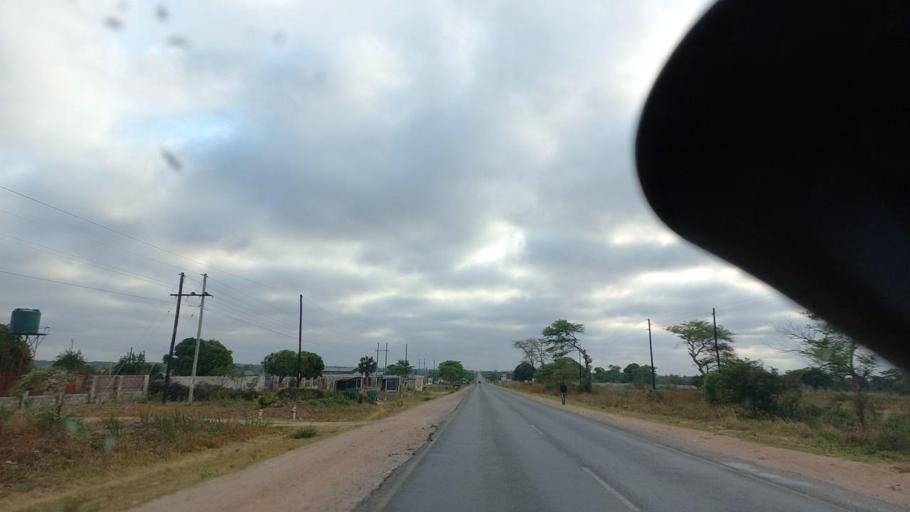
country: ZM
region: Lusaka
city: Chongwe
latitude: -15.3542
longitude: 28.4854
